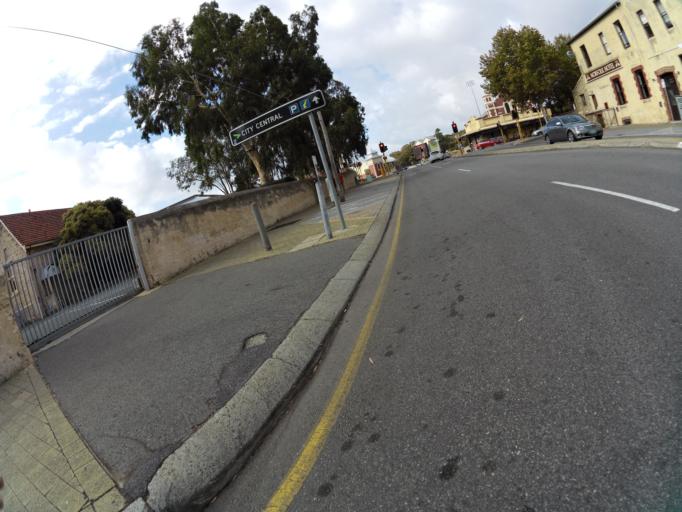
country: AU
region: Western Australia
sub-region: Fremantle
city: South Fremantle
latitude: -32.0571
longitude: 115.7490
